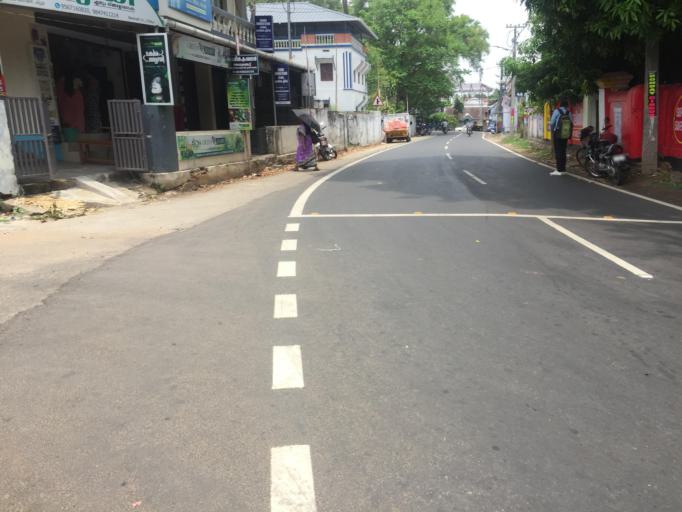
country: IN
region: Kerala
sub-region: Palakkad district
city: Chittur
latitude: 10.7028
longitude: 76.7395
